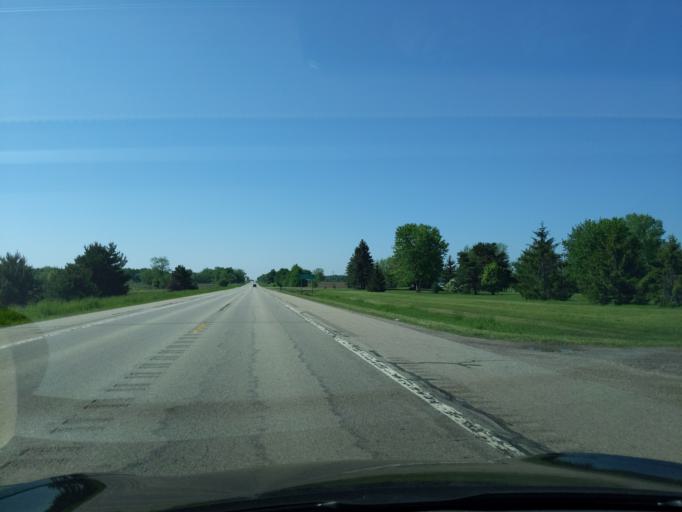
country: US
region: Michigan
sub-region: Ingham County
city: Webberville
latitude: 42.5871
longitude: -84.1931
